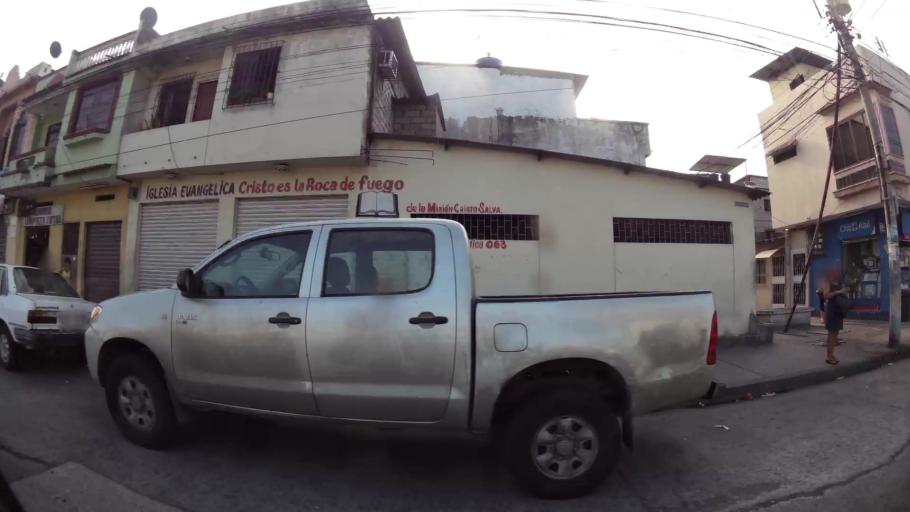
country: EC
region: Guayas
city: Eloy Alfaro
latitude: -2.1279
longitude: -79.9011
